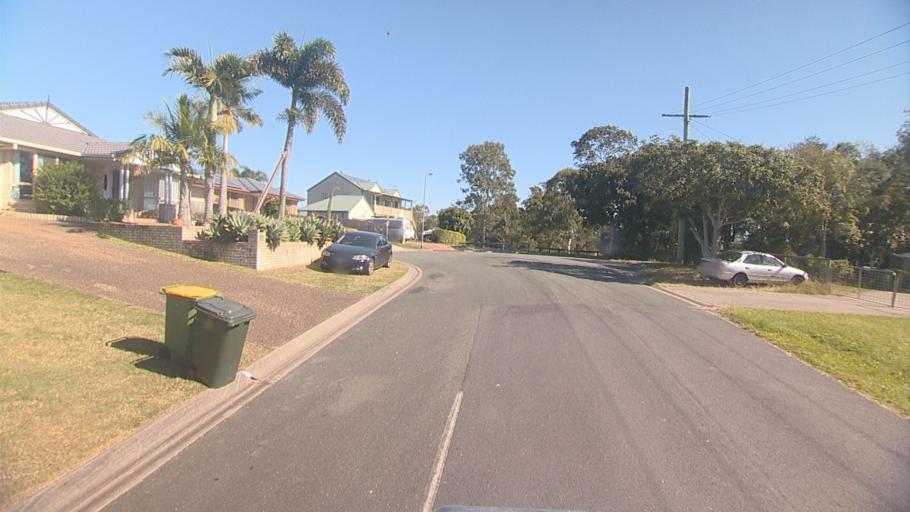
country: AU
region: Queensland
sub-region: Logan
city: Beenleigh
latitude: -27.6939
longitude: 153.2054
